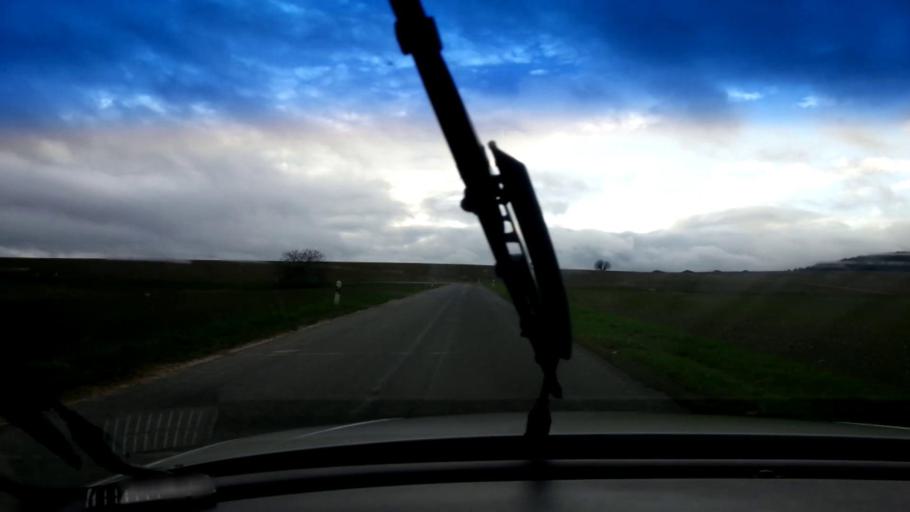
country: DE
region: Bavaria
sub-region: Upper Franconia
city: Zapfendorf
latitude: 50.0290
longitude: 10.9696
